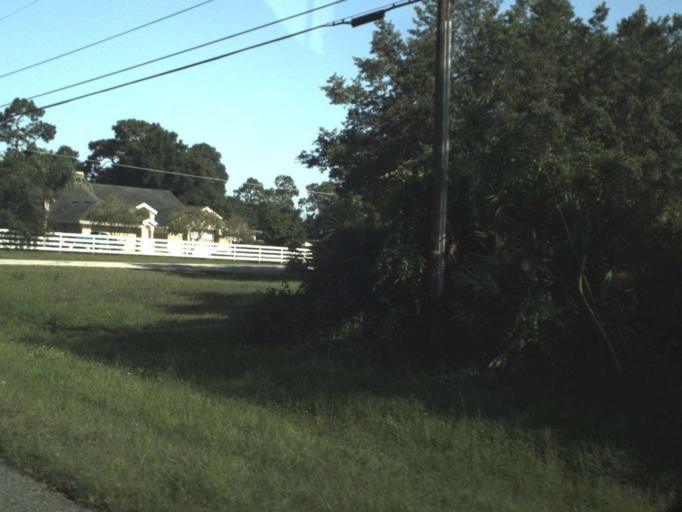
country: US
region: Florida
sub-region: Seminole County
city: Geneva
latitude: 28.7279
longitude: -81.1061
